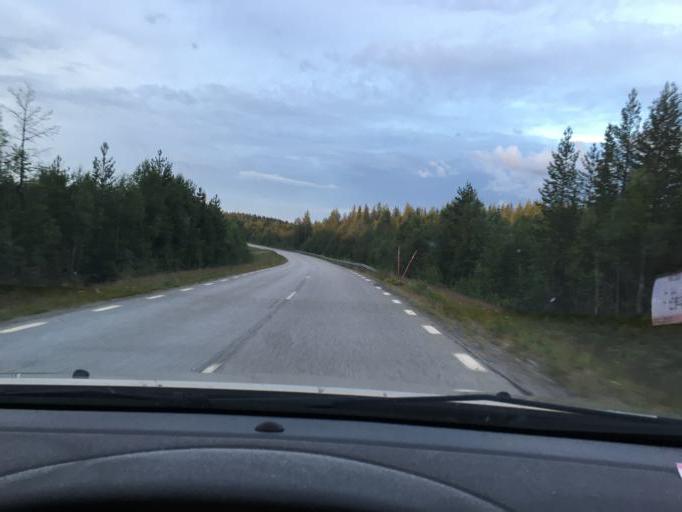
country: SE
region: Norrbotten
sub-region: Lulea Kommun
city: Ranea
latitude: 66.0483
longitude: 22.2624
